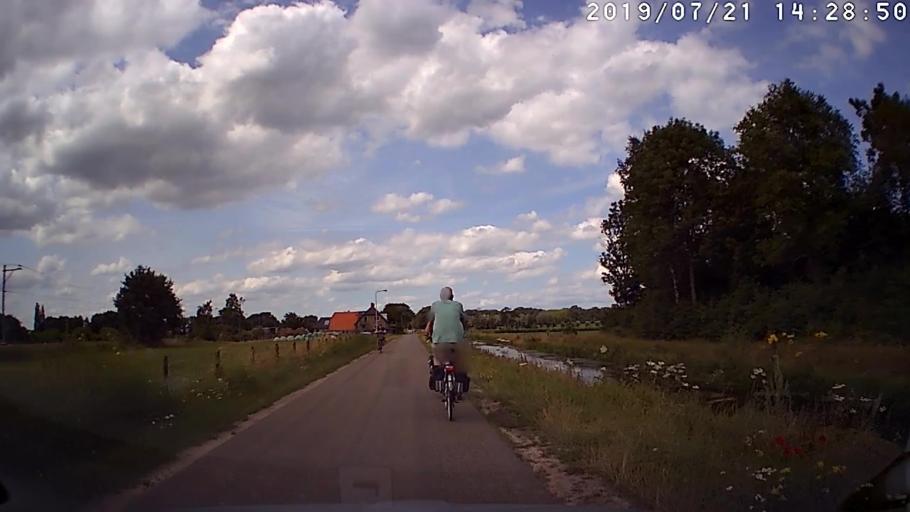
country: NL
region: Overijssel
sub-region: Gemeente Raalte
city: Heino
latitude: 52.4405
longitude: 6.2013
